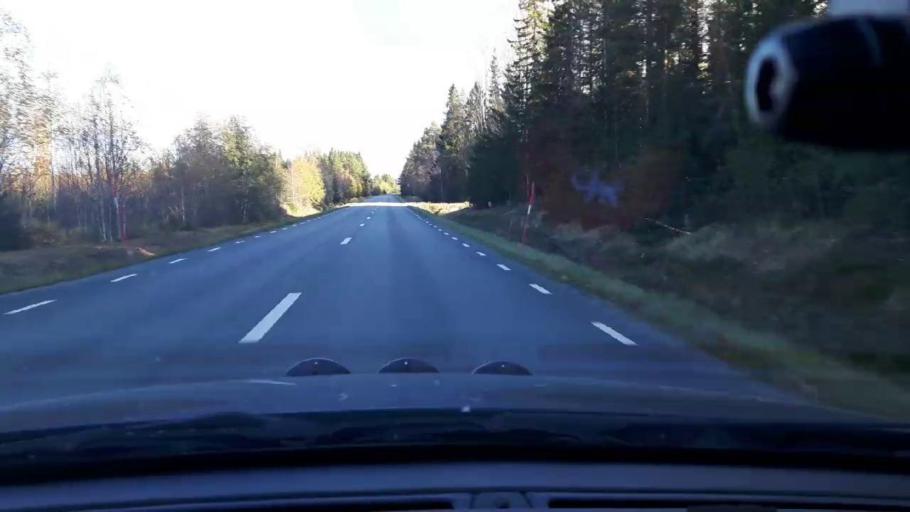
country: SE
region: Jaemtland
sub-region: Bergs Kommun
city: Hoverberg
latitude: 62.9857
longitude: 14.4400
